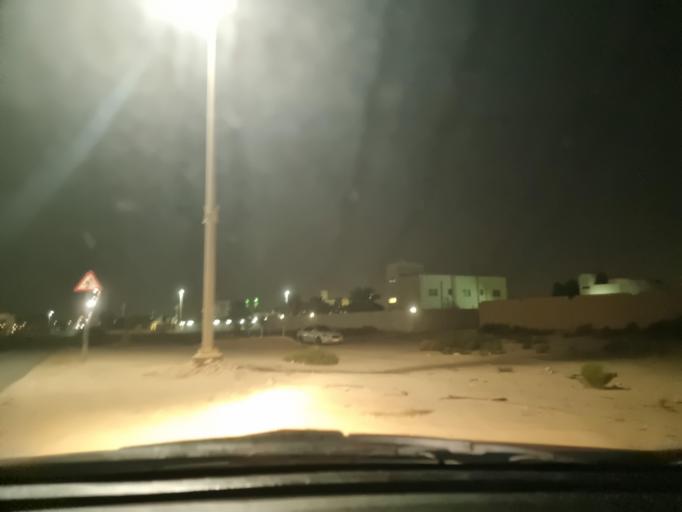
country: AE
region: Abu Dhabi
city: Abu Dhabi
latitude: 24.3823
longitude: 54.6999
